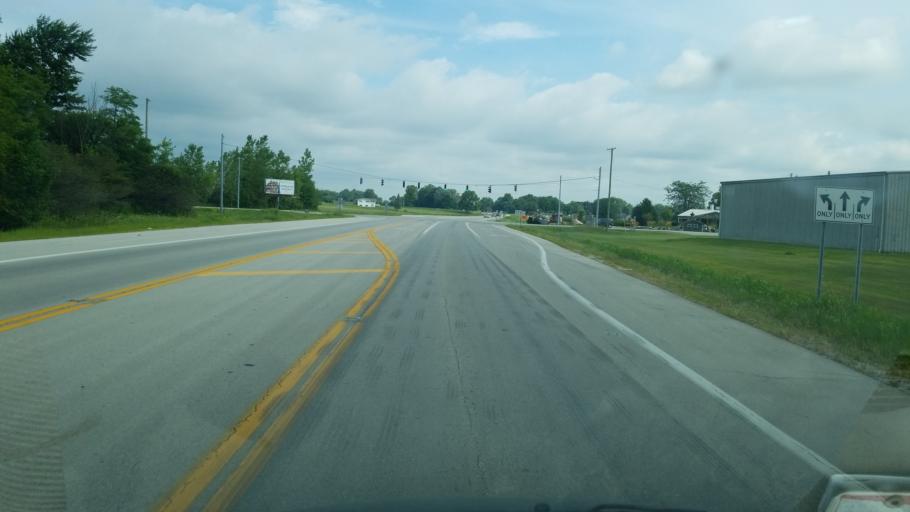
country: US
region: Ohio
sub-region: Sandusky County
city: Ballville
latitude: 41.2904
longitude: -83.1712
